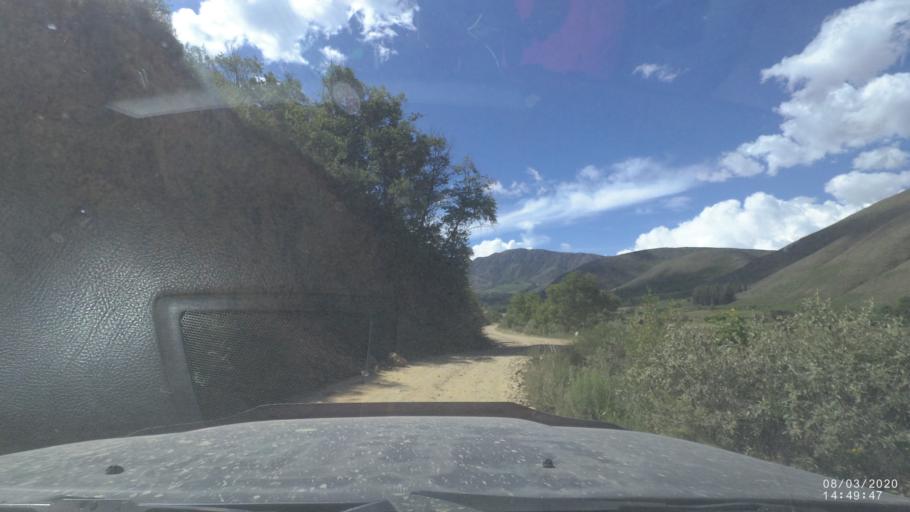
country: BO
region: Cochabamba
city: Totora
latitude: -17.6995
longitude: -65.3453
